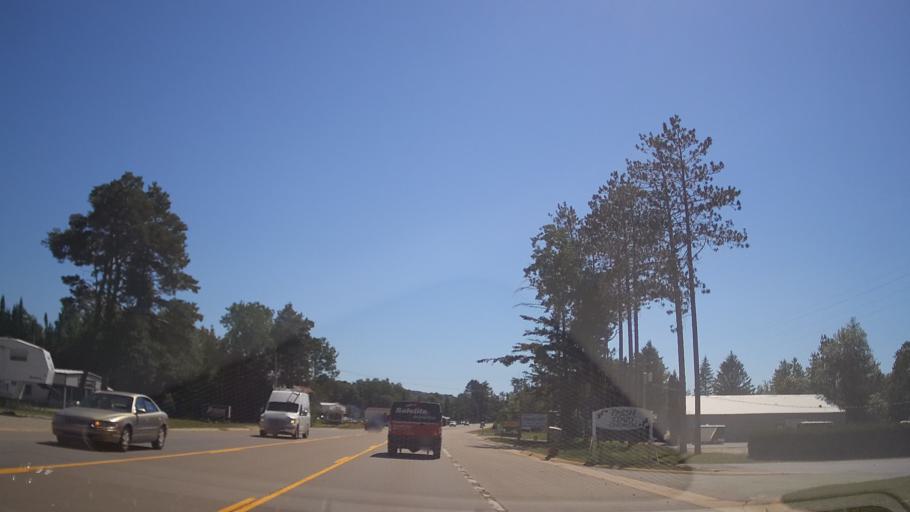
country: US
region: Michigan
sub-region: Emmet County
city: Petoskey
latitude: 45.4062
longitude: -84.8718
